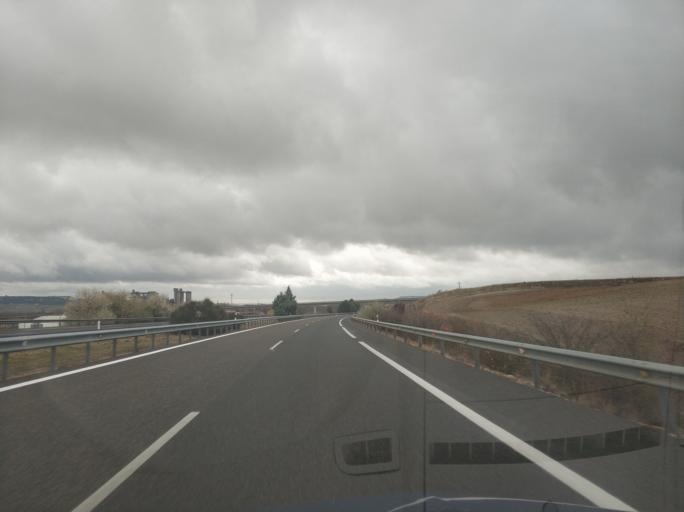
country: ES
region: Castille and Leon
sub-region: Provincia de Palencia
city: Soto de Cerrato
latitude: 41.9542
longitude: -4.4608
